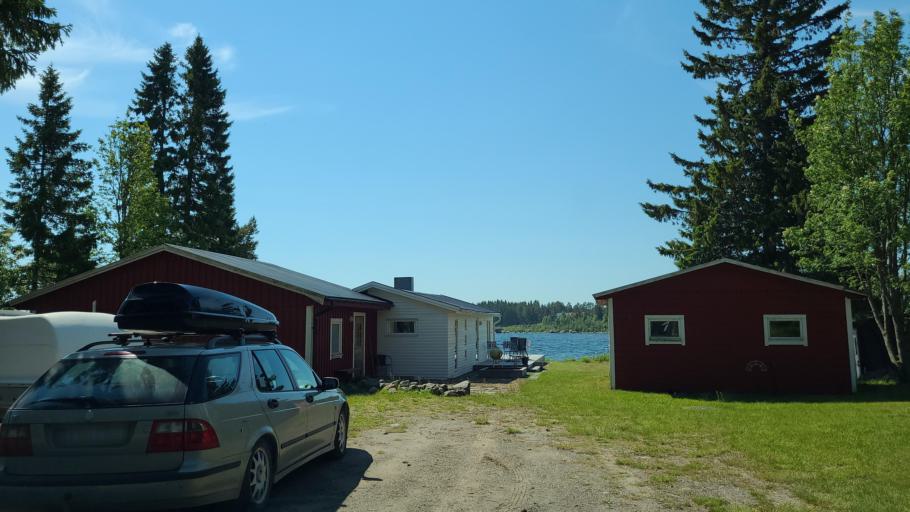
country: SE
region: Vaesterbotten
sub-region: Robertsfors Kommun
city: Robertsfors
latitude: 64.1383
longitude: 20.9633
